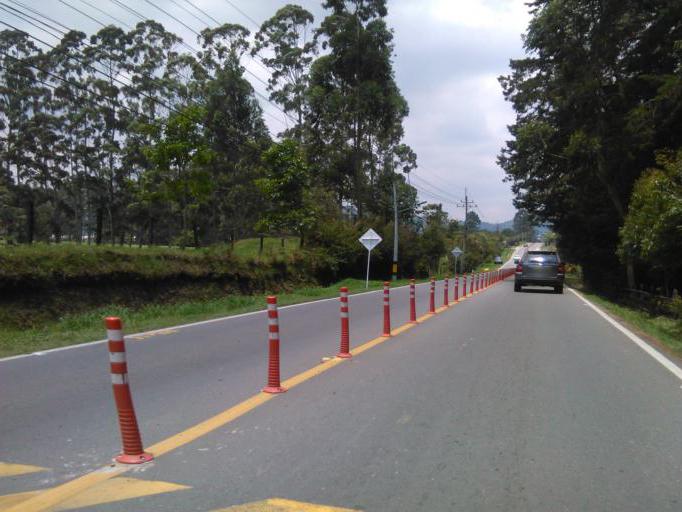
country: CO
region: Antioquia
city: La Ceja
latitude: 6.0225
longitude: -75.4113
